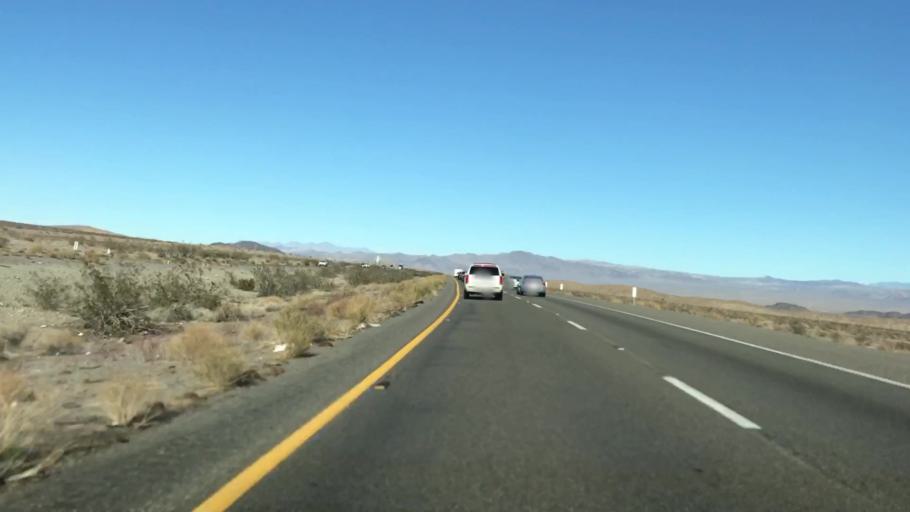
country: US
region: California
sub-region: San Bernardino County
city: Fort Irwin
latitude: 35.2032
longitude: -116.1187
